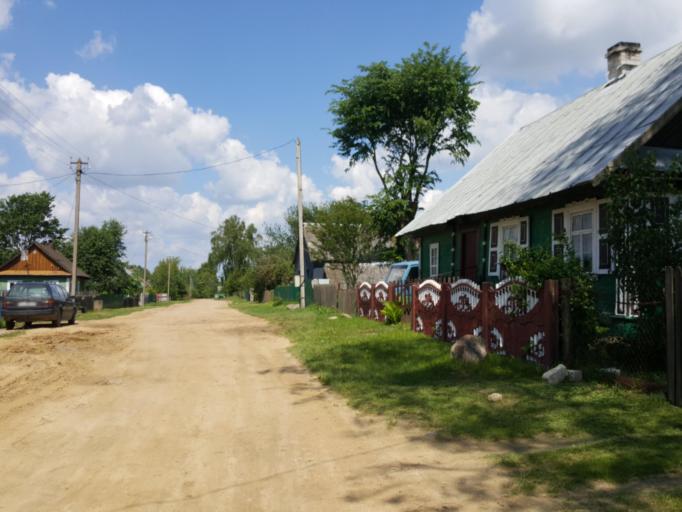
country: BY
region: Brest
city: Kamyanyets
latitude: 52.3991
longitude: 23.7562
